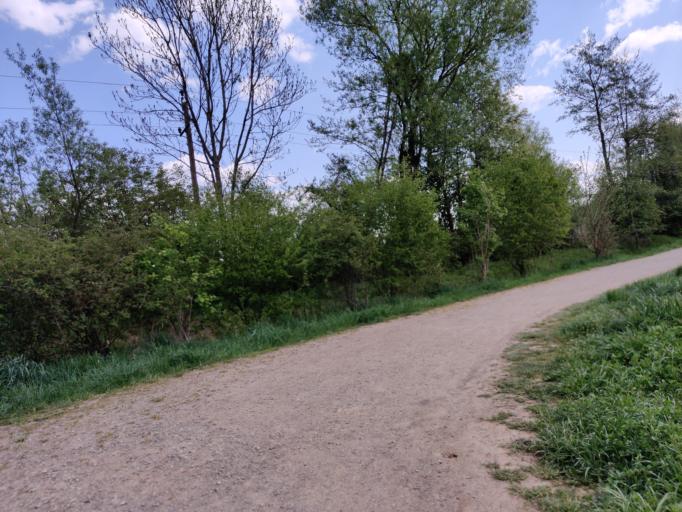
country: AT
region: Styria
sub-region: Graz Stadt
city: Wetzelsdorf
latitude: 47.0400
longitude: 15.3882
